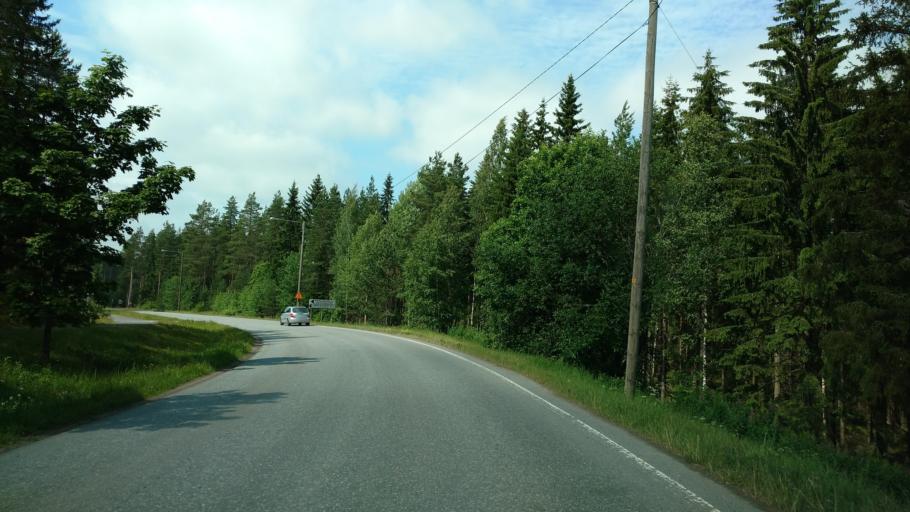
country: FI
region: Haeme
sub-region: Forssa
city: Ypaejae
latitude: 60.8078
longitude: 23.3205
